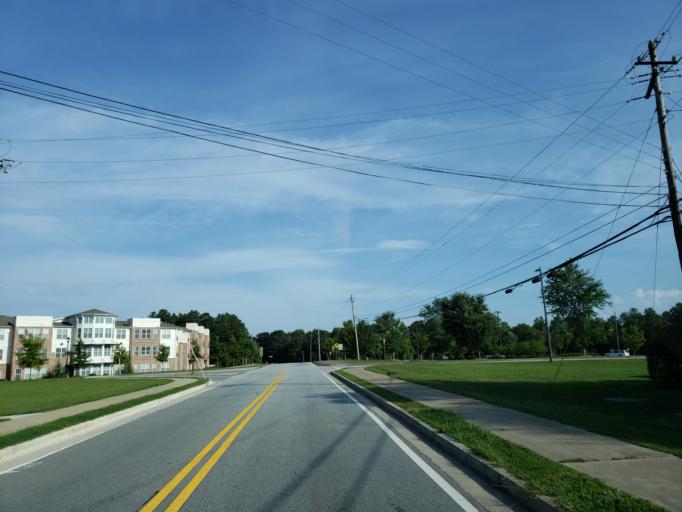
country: US
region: Georgia
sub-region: Cobb County
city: Powder Springs
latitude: 33.8687
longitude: -84.7012
